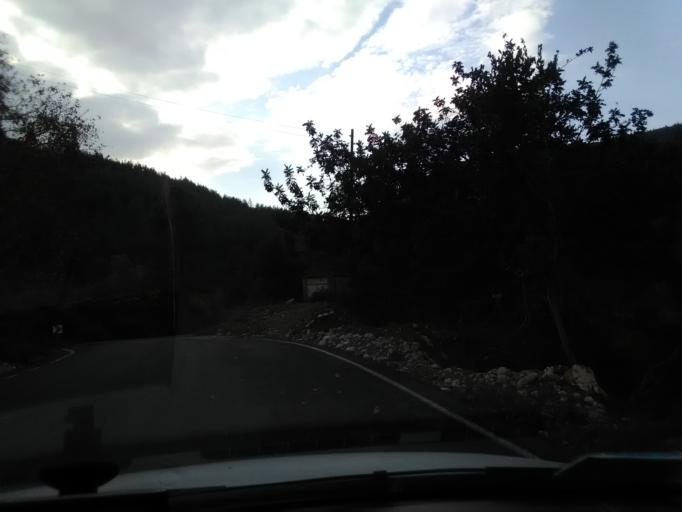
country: TR
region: Antalya
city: Gazipasa
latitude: 36.2855
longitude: 32.3730
